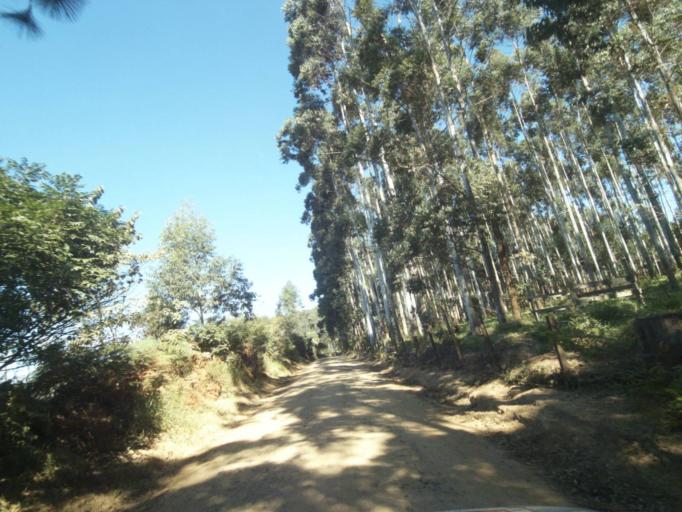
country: BR
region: Parana
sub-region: Tibagi
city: Tibagi
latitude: -24.5497
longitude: -50.6209
